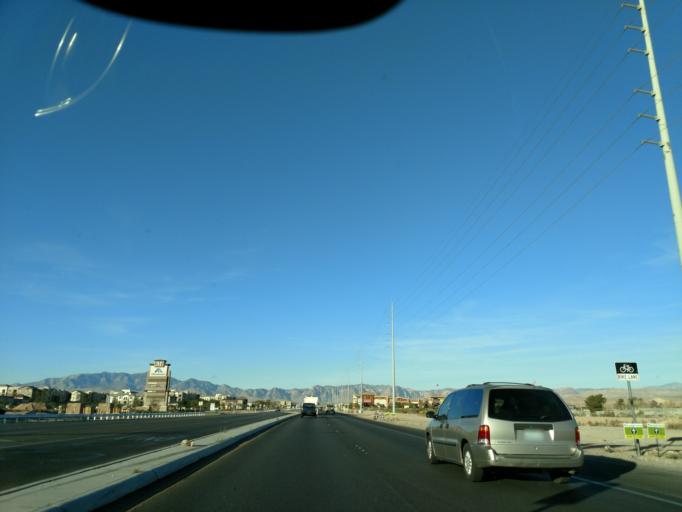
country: US
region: Nevada
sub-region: Clark County
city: Enterprise
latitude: 36.0202
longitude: -115.2612
